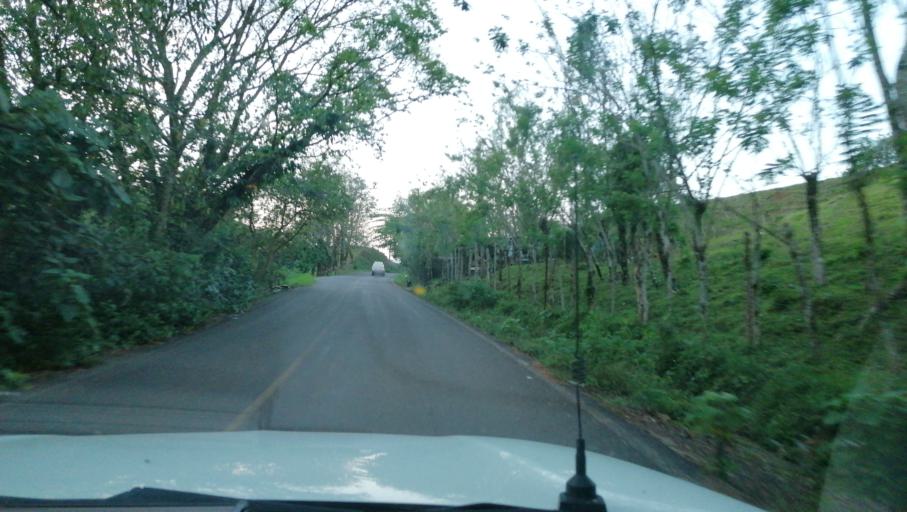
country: MX
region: Chiapas
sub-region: Ostuacan
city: Nuevo Juan del Grijalva
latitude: 17.4269
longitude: -93.3503
